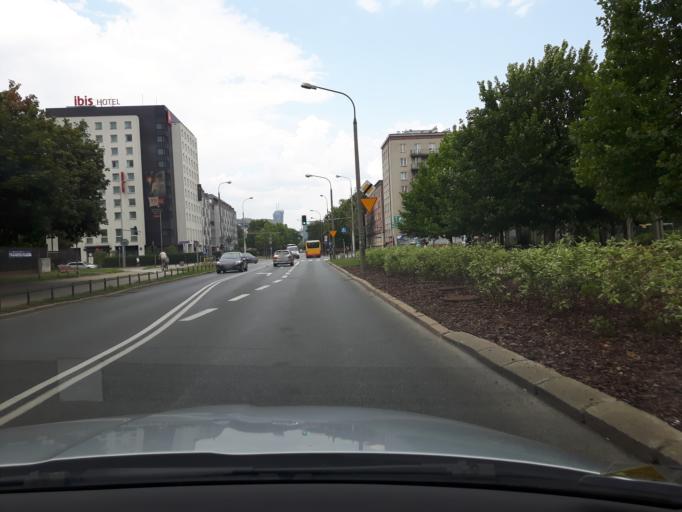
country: PL
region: Masovian Voivodeship
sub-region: Warszawa
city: Ochota
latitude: 52.2132
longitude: 20.9678
